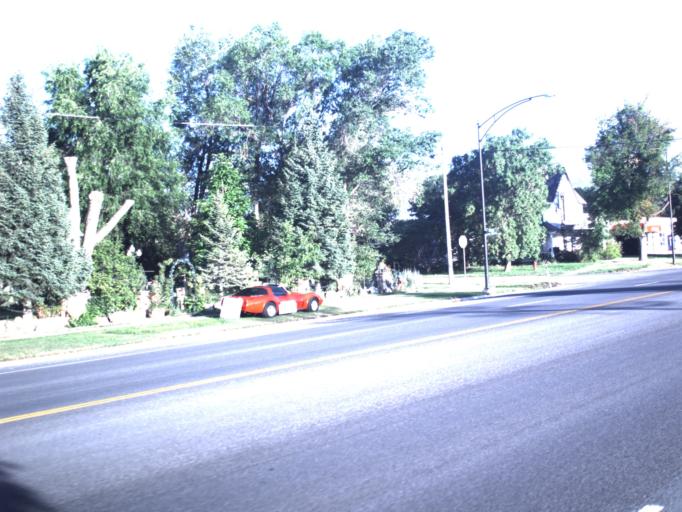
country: US
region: Utah
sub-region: Sanpete County
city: Mount Pleasant
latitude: 39.5516
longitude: -111.4555
